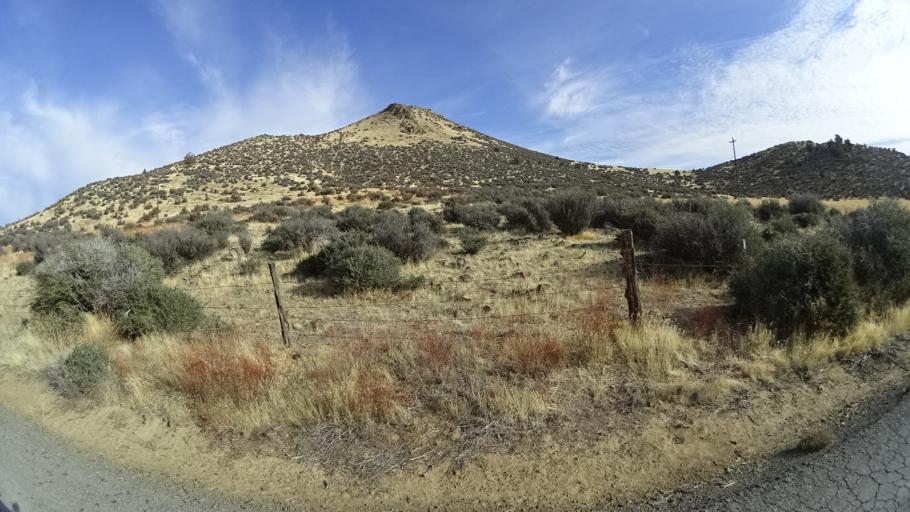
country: US
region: California
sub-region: Siskiyou County
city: Montague
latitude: 41.7093
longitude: -122.5194
